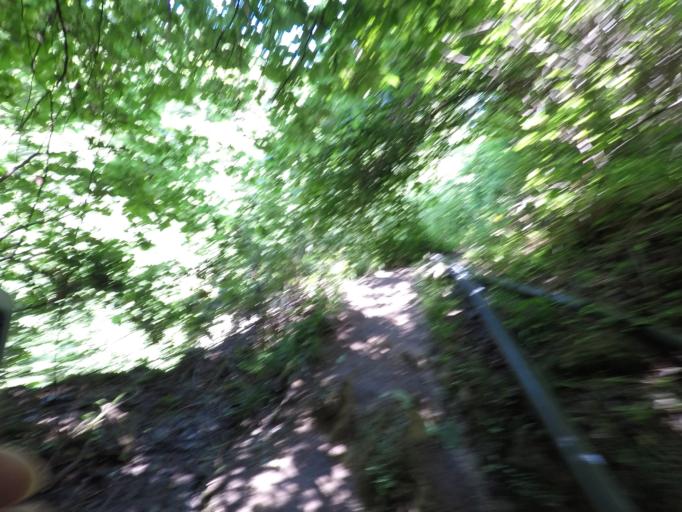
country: AZ
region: Qakh Rayon
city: Cinarli
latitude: 41.4926
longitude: 46.8587
